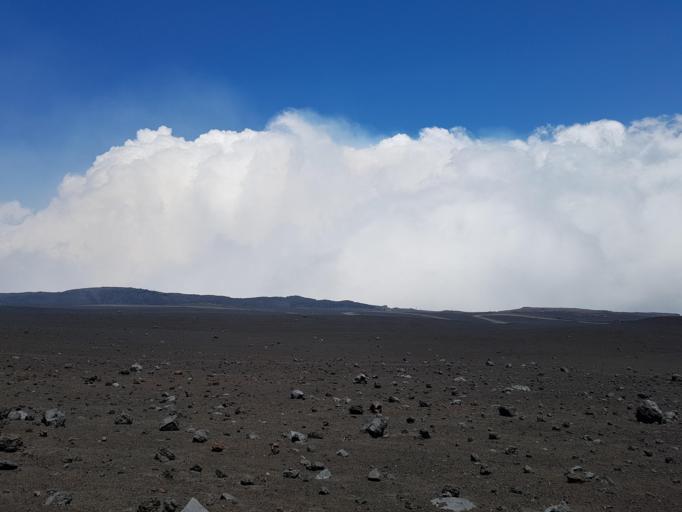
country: IT
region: Sicily
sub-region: Catania
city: Lavinaio-Monterosso
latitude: 37.6336
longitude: 15.0900
